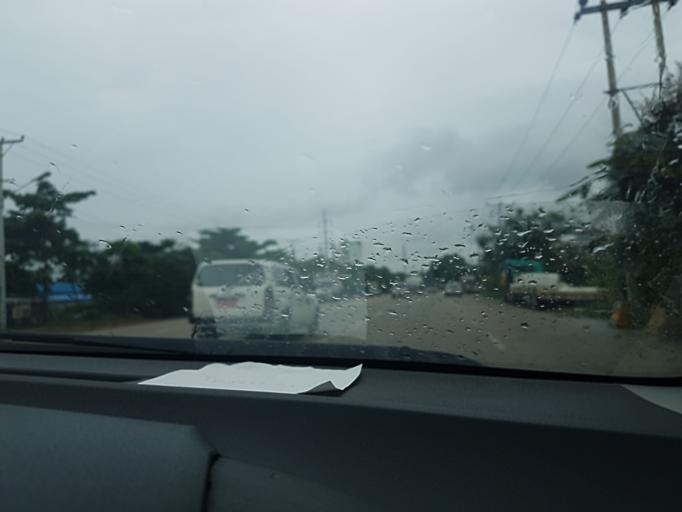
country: MM
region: Yangon
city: Syriam
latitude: 16.7925
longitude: 96.2189
